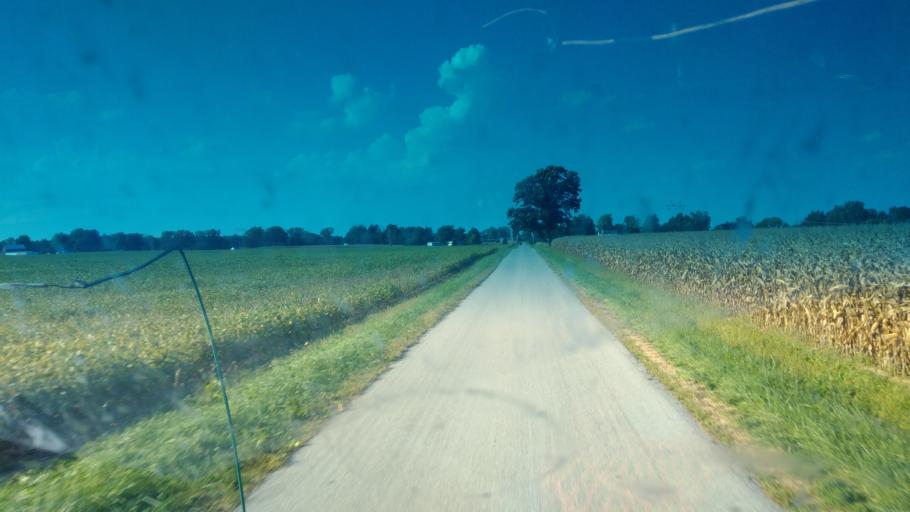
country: US
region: Ohio
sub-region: Wyandot County
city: Upper Sandusky
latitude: 40.9265
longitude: -83.1893
